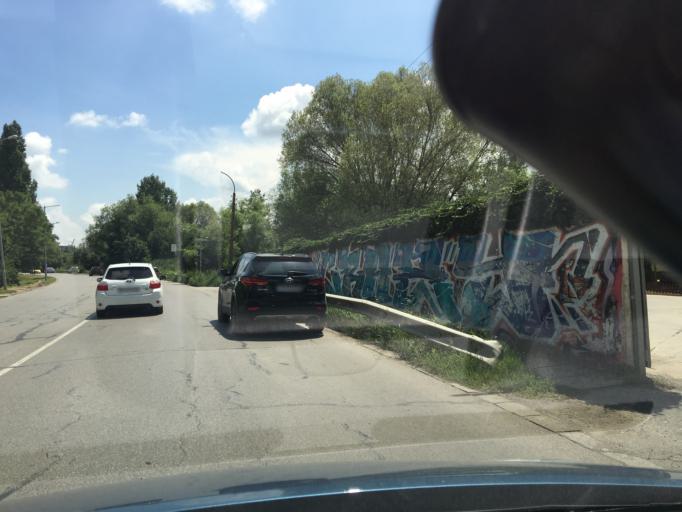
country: BG
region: Sofia-Capital
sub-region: Stolichna Obshtina
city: Sofia
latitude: 42.6590
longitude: 23.3063
